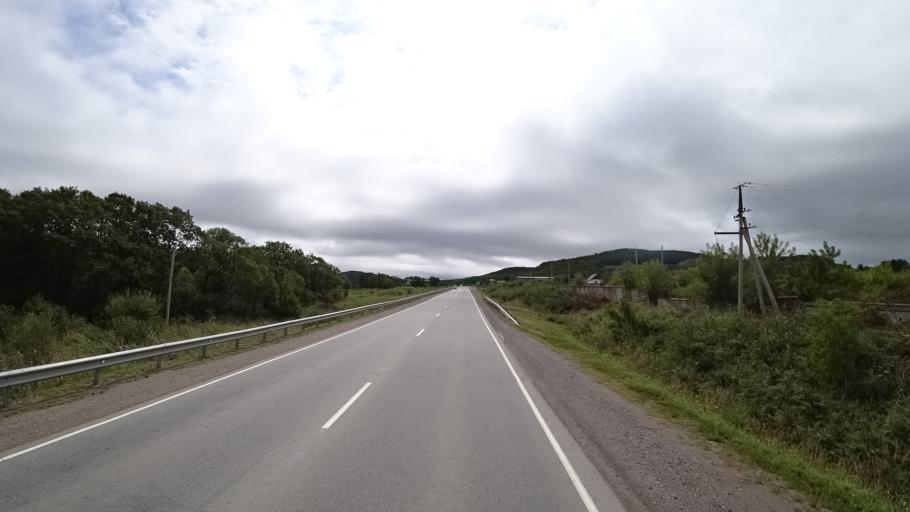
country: RU
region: Primorskiy
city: Monastyrishche
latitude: 44.1682
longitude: 132.4408
